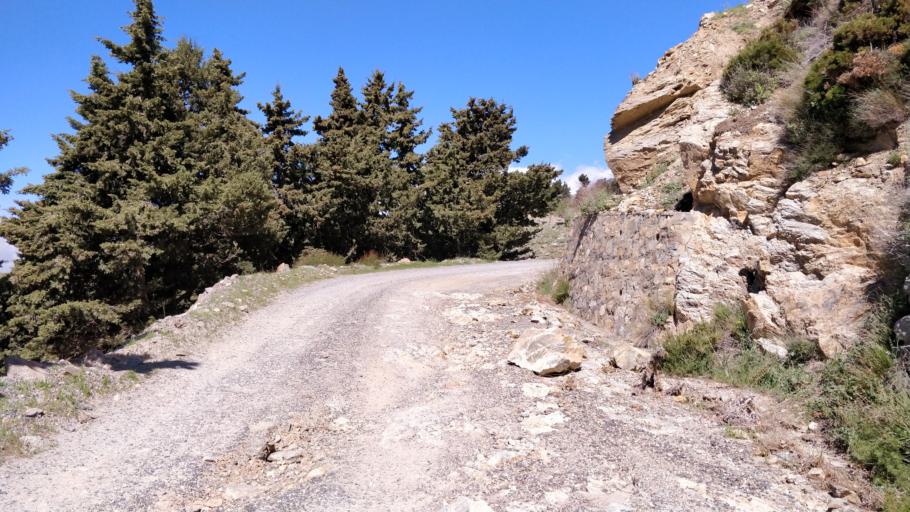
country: ES
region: Andalusia
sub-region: Provincia de Granada
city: Soportujar
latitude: 36.9346
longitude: -3.4016
